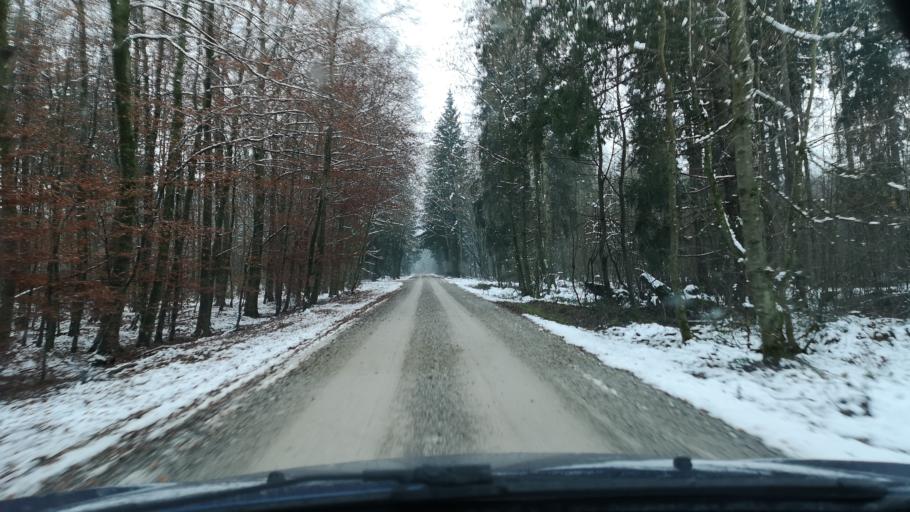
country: DE
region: Bavaria
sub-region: Upper Bavaria
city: Anzing
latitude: 48.1388
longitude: 11.8689
